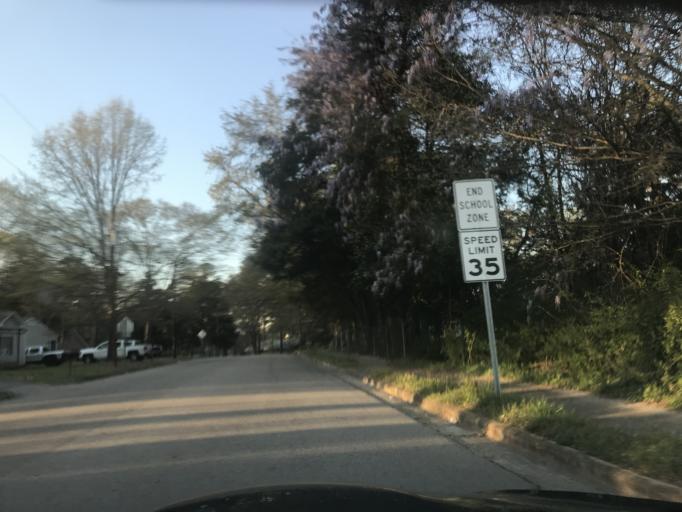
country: US
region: North Carolina
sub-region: Wake County
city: Raleigh
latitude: 35.7753
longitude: -78.6058
